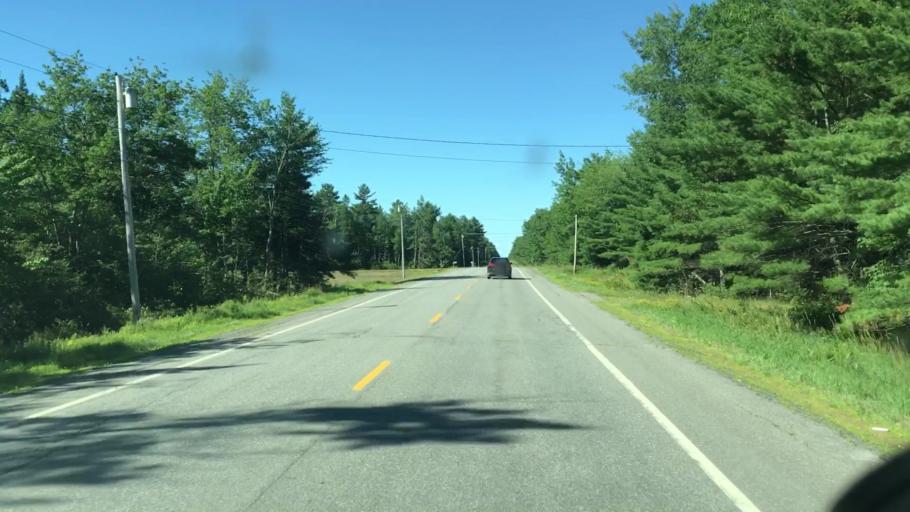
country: US
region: Maine
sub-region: Penobscot County
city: Enfield
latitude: 45.3220
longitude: -68.5977
